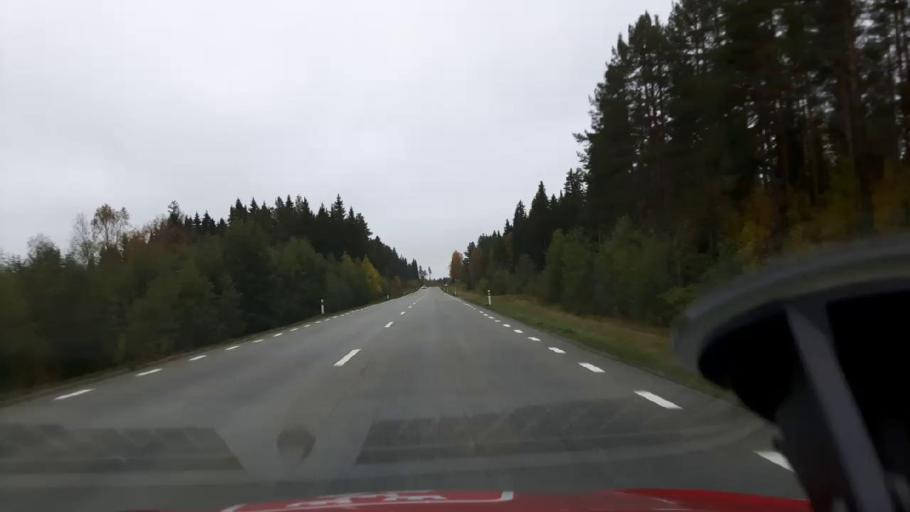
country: SE
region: Jaemtland
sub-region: Bergs Kommun
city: Hoverberg
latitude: 62.7211
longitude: 14.4153
